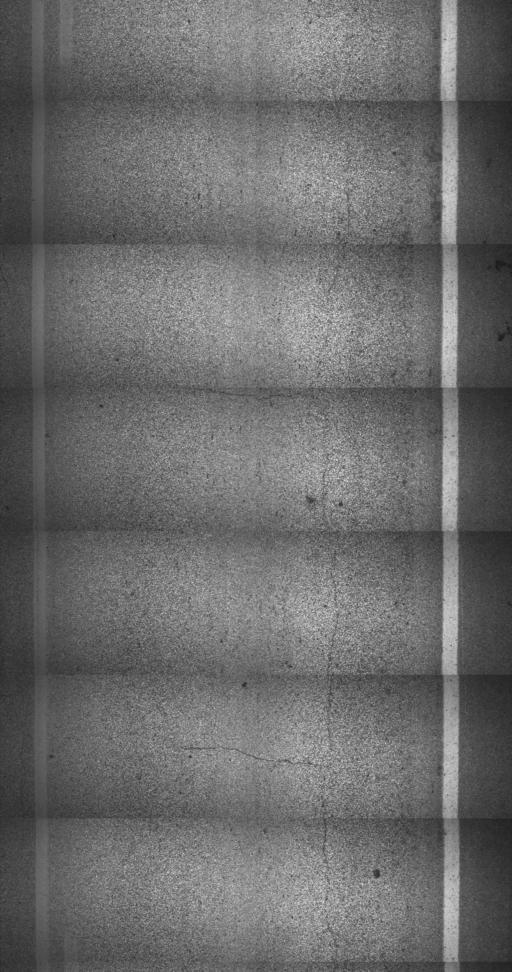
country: US
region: Vermont
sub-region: Windsor County
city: Chester
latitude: 43.1811
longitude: -72.8176
